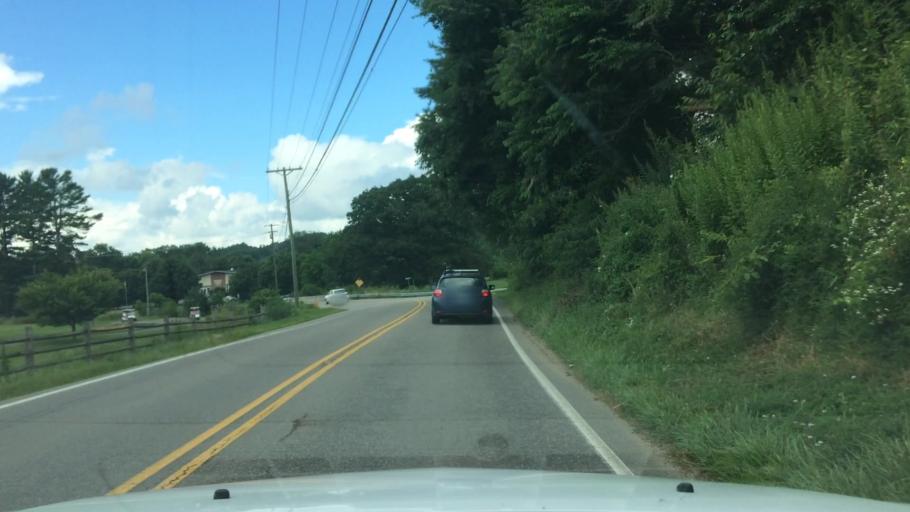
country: US
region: North Carolina
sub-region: Watauga County
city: Boone
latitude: 36.2020
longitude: -81.6471
